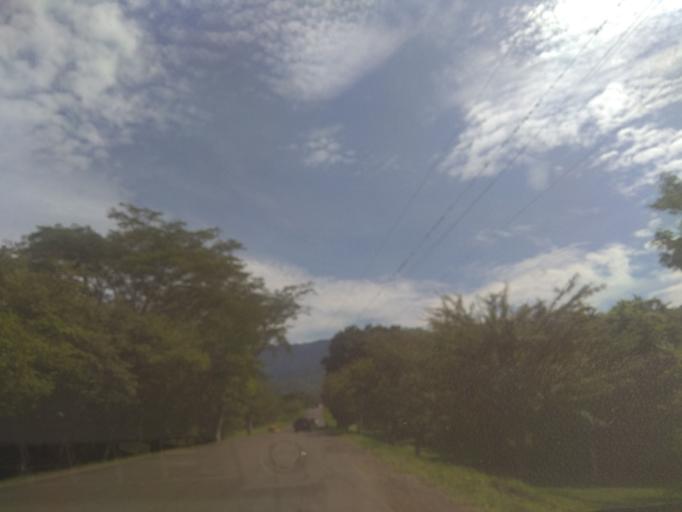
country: HN
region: Intibuca
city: Jesus de Otoro
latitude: 14.4752
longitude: -87.9945
